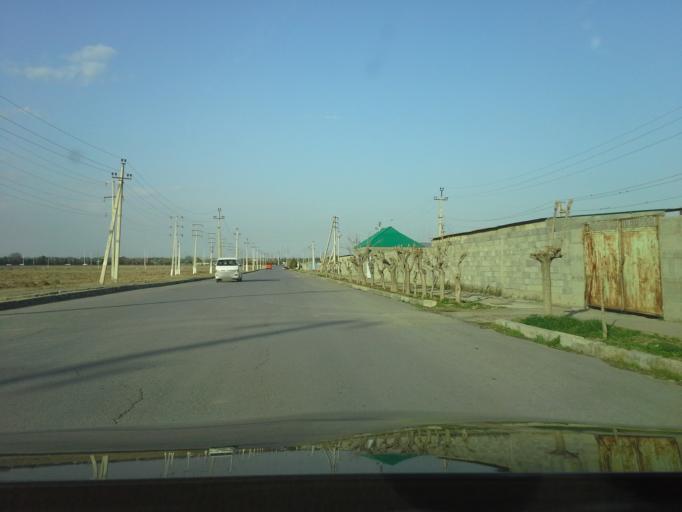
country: TM
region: Ahal
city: Abadan
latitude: 38.0278
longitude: 58.2227
